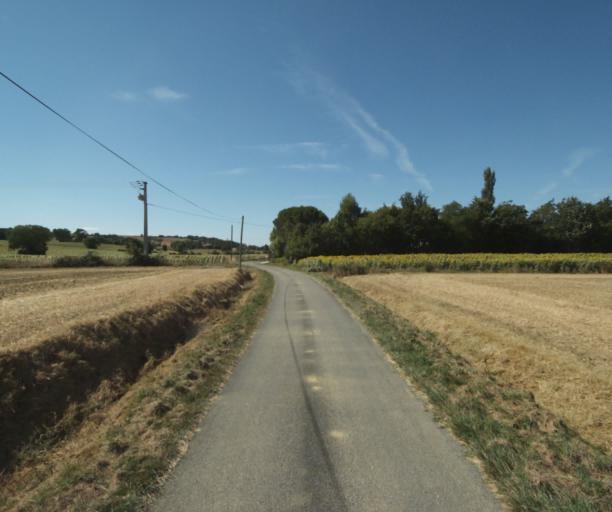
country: FR
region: Midi-Pyrenees
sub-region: Departement de la Haute-Garonne
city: Saint-Felix-Lauragais
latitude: 43.5050
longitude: 1.8932
